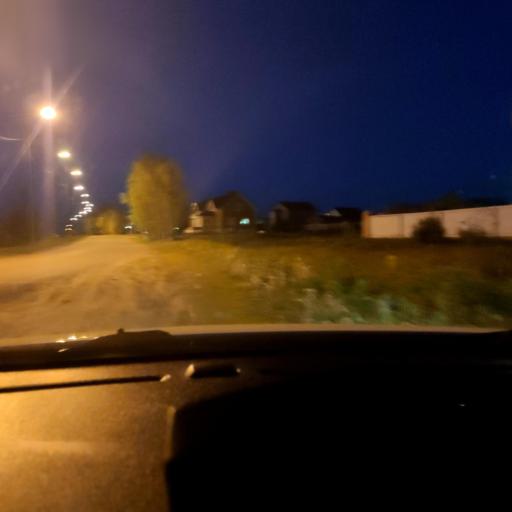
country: RU
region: Tatarstan
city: Vysokaya Gora
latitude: 55.8438
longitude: 49.3292
